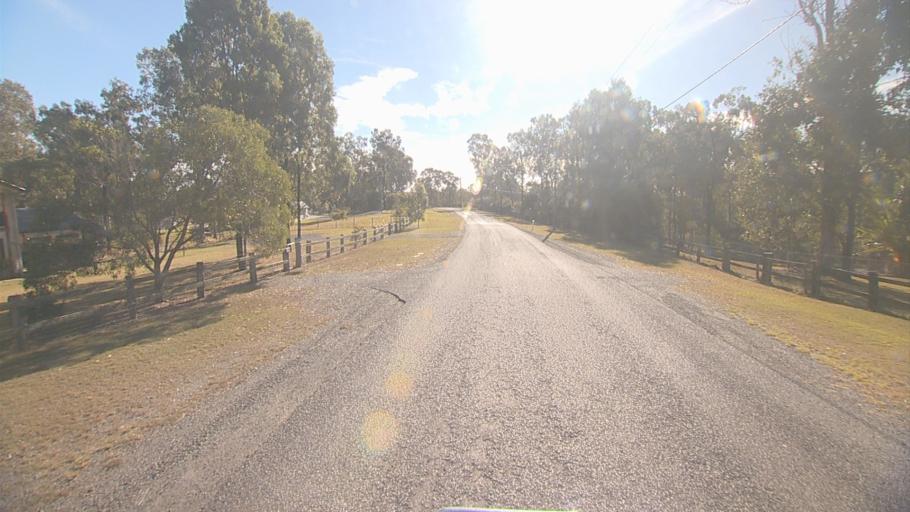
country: AU
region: Queensland
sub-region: Ipswich
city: Springfield Lakes
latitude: -27.7020
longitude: 152.9293
